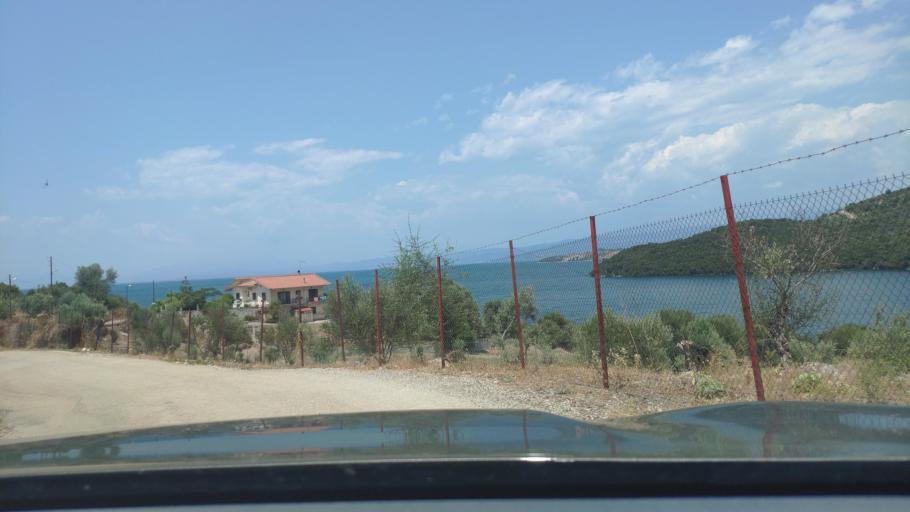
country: GR
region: West Greece
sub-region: Nomos Aitolias kai Akarnanias
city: Amfilochia
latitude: 38.8666
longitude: 21.0750
